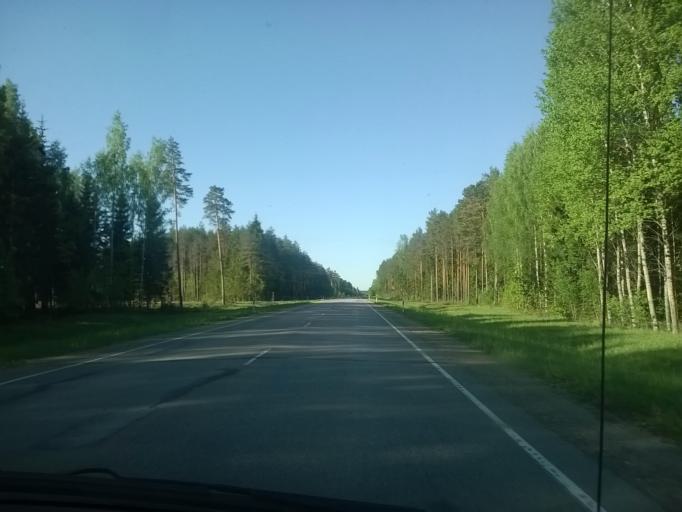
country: EE
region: Valgamaa
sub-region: Valga linn
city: Valga
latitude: 57.8663
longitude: 26.1464
